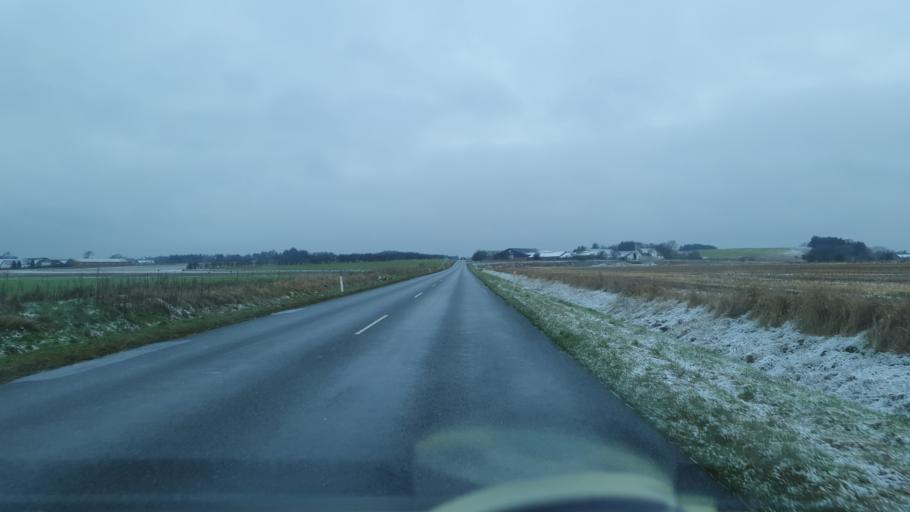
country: DK
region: North Denmark
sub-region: Jammerbugt Kommune
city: Brovst
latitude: 57.1198
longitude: 9.4956
